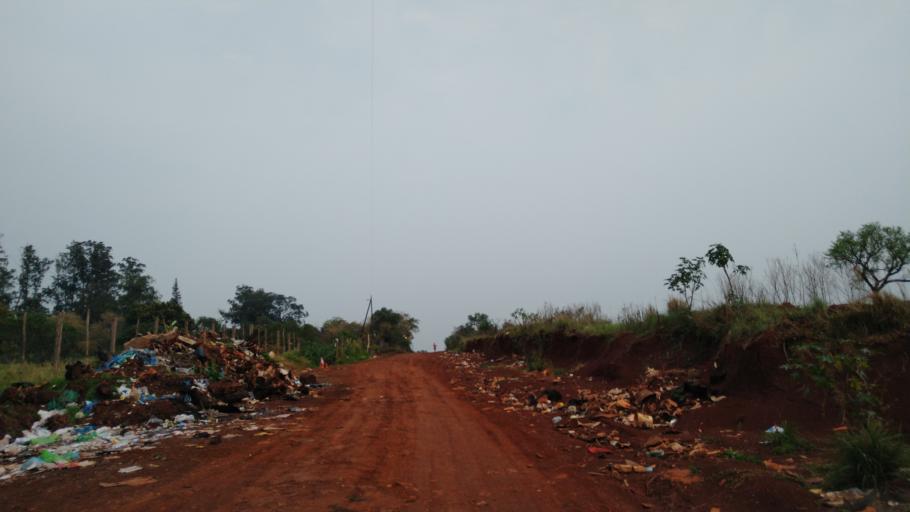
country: AR
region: Misiones
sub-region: Departamento de Capital
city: Posadas
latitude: -27.4473
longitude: -55.9383
